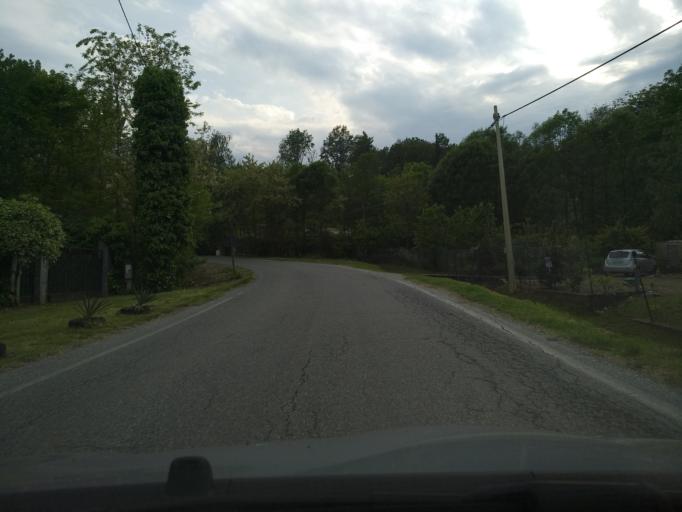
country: IT
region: Piedmont
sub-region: Provincia di Torino
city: Roletto
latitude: 44.9288
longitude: 7.3381
